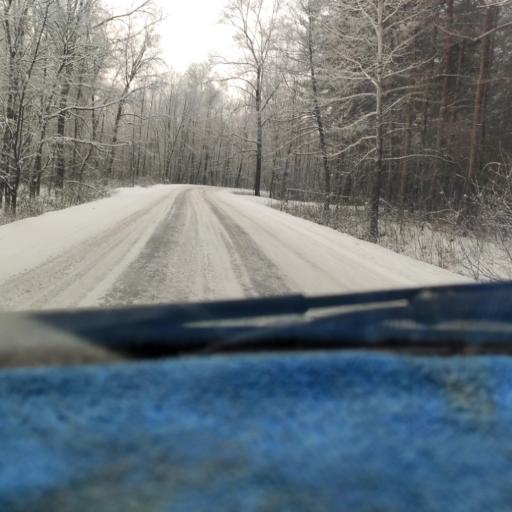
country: RU
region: Bashkortostan
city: Avdon
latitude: 54.6739
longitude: 55.8432
